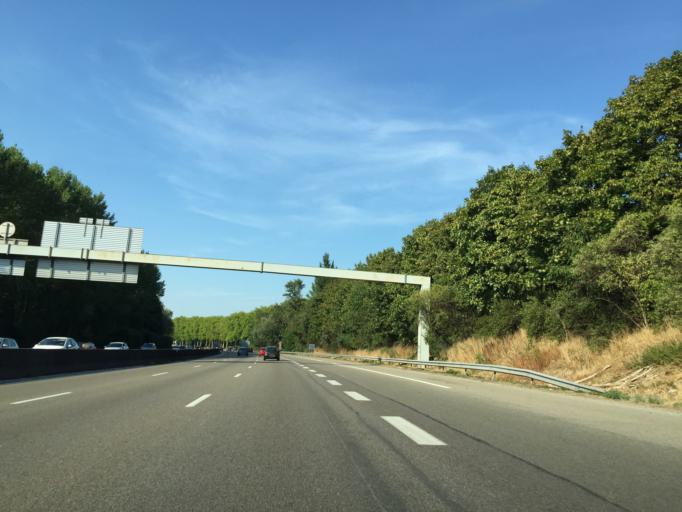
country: FR
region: Alsace
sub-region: Departement du Bas-Rhin
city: Ostwald
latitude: 48.5487
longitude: 7.7304
